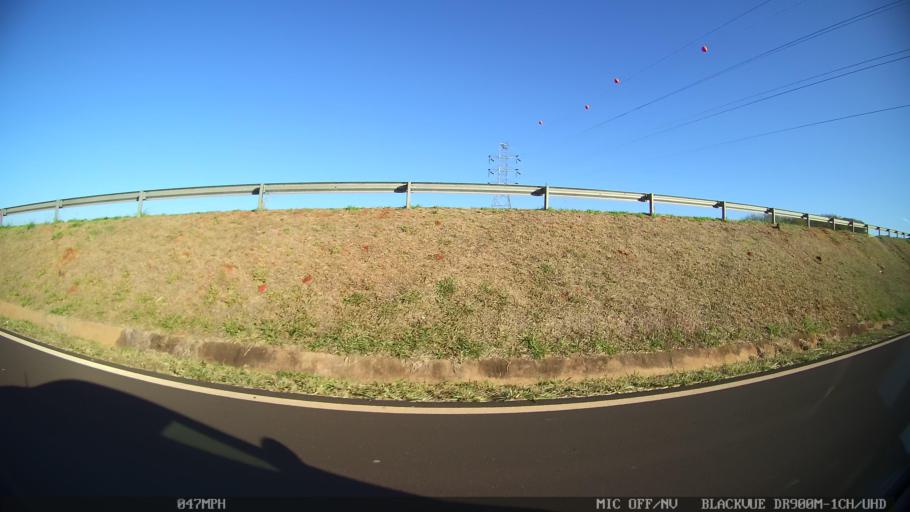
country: BR
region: Sao Paulo
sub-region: Guapiacu
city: Guapiacu
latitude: -20.7723
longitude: -49.2244
